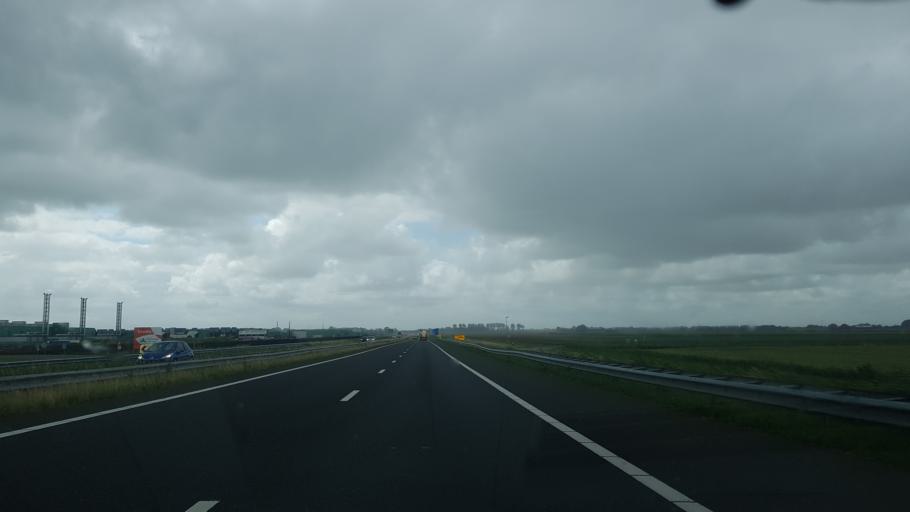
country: NL
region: North Holland
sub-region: Gemeente Medemblik
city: Opperdoes
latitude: 52.7698
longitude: 5.0344
